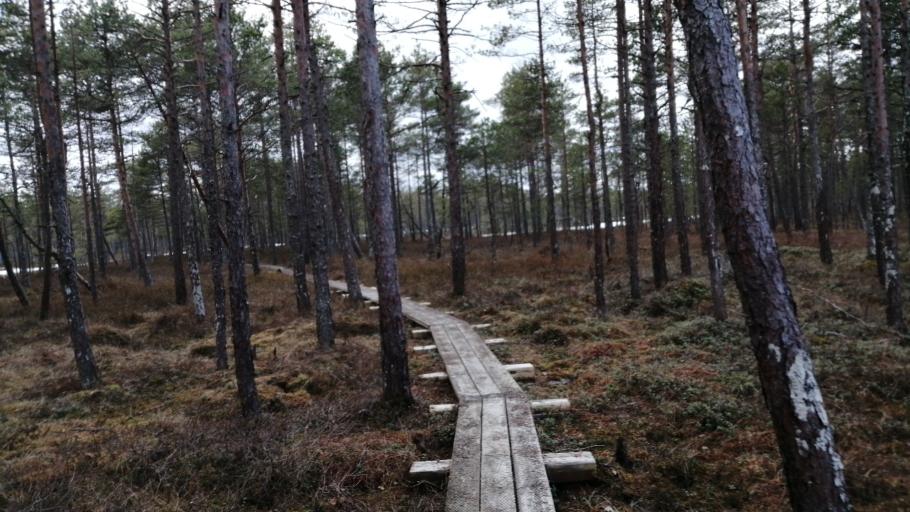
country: EE
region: Ida-Virumaa
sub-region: Kohtla-Nomme vald
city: Kohtla-Nomme
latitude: 59.1719
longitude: 27.2813
